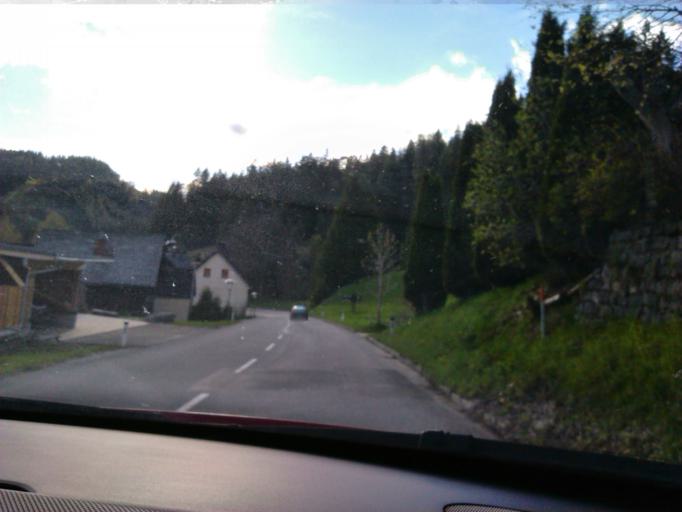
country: AT
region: Styria
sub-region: Politischer Bezirk Bruck-Muerzzuschlag
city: Muerzsteg
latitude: 47.7730
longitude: 15.5058
